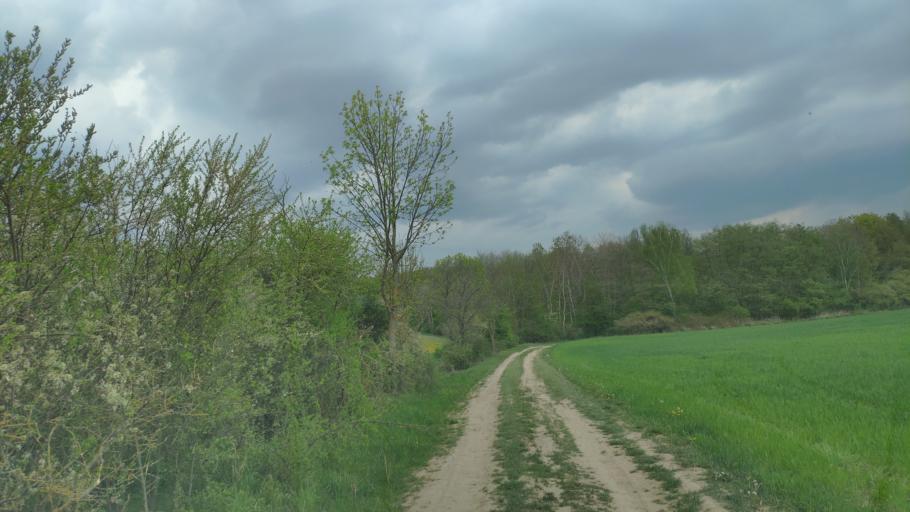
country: SK
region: Kosicky
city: Moldava nad Bodvou
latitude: 48.6170
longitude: 21.0402
